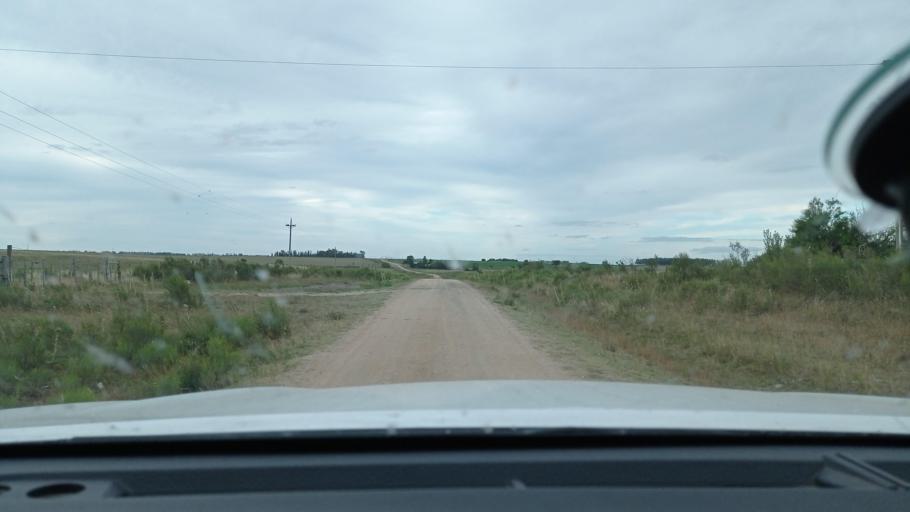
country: UY
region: Florida
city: Casupa
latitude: -34.1251
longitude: -55.7741
